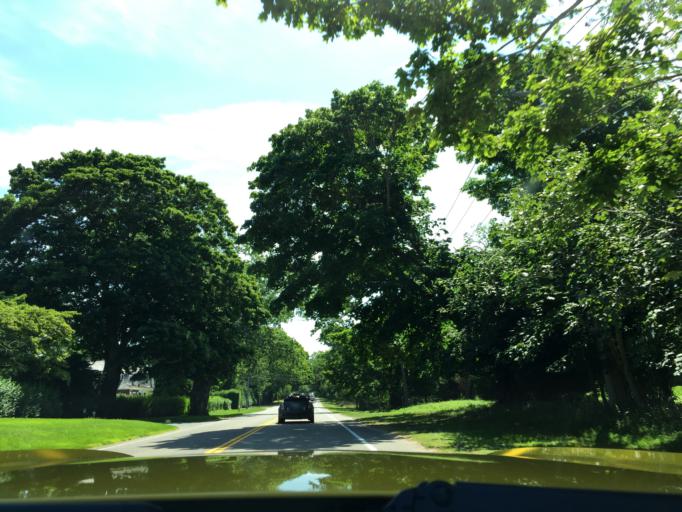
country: US
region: New York
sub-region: Suffolk County
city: Bridgehampton
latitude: 40.9311
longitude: -72.2994
